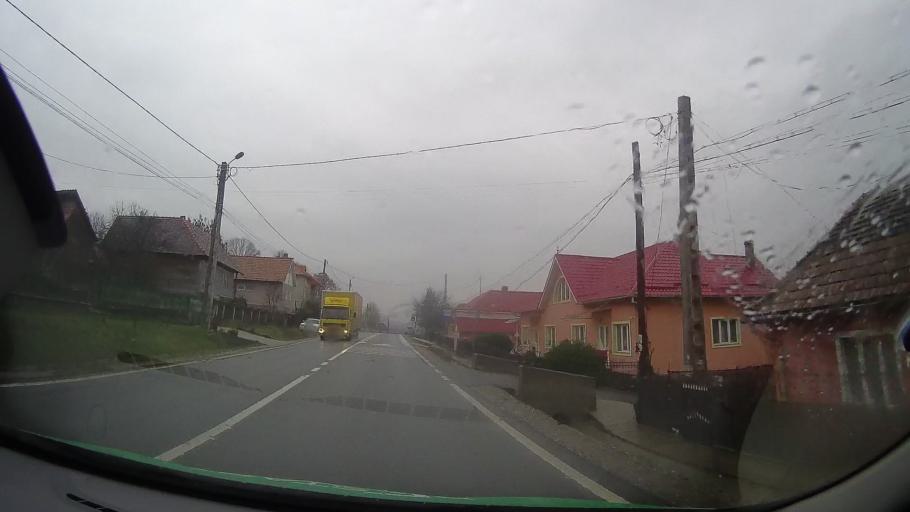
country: RO
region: Bistrita-Nasaud
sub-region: Comuna Galatii Bistritei
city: Galatii Bistritei
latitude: 46.9928
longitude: 24.4209
